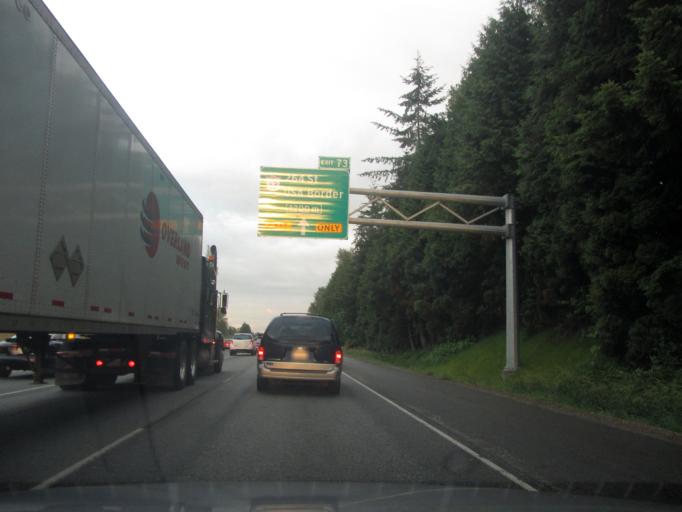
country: CA
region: British Columbia
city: Aldergrove
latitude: 49.1082
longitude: -122.5105
